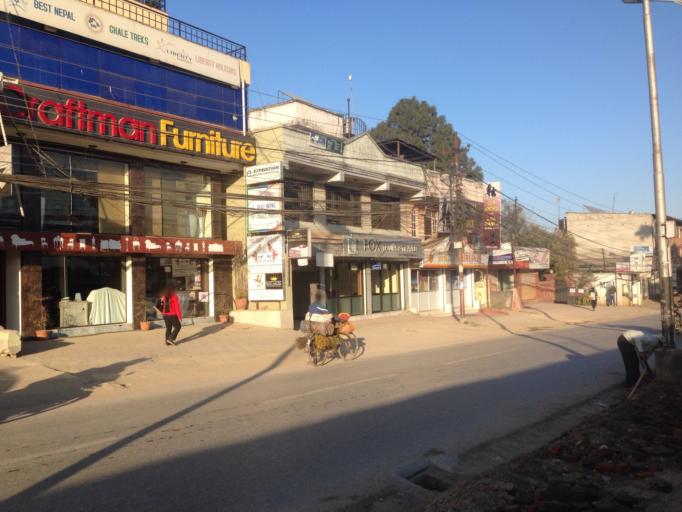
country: NP
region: Central Region
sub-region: Bagmati Zone
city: Kathmandu
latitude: 27.7180
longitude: 85.3206
